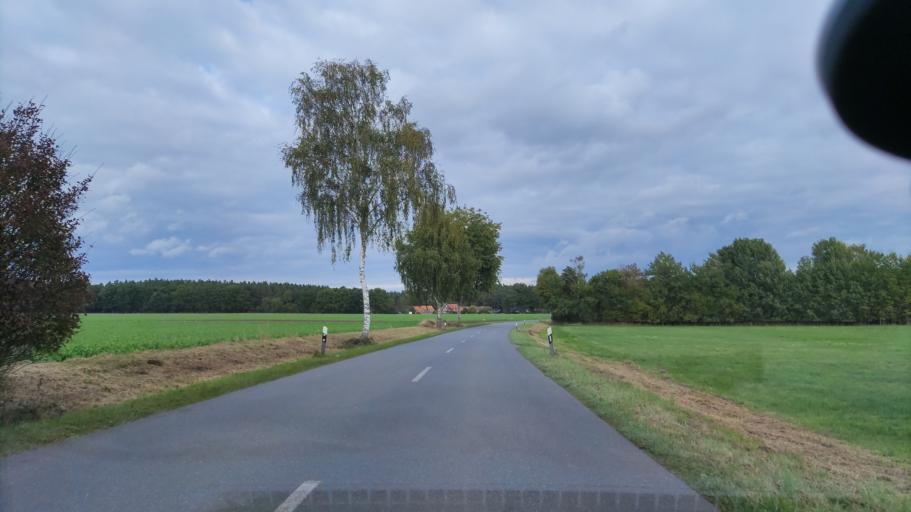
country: DE
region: Lower Saxony
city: Bad Bevensen
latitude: 53.0648
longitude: 10.6153
